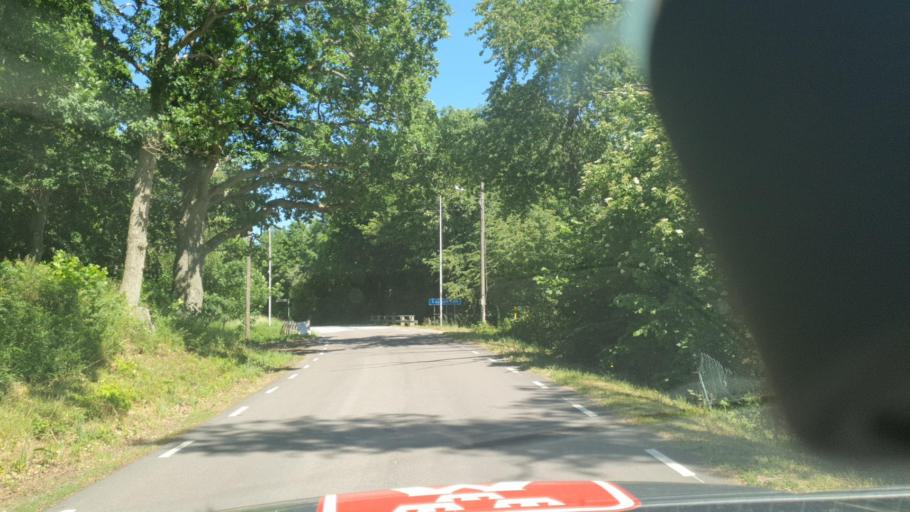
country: SE
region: Kalmar
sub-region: Torsas Kommun
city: Torsas
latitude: 56.3000
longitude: 15.9992
